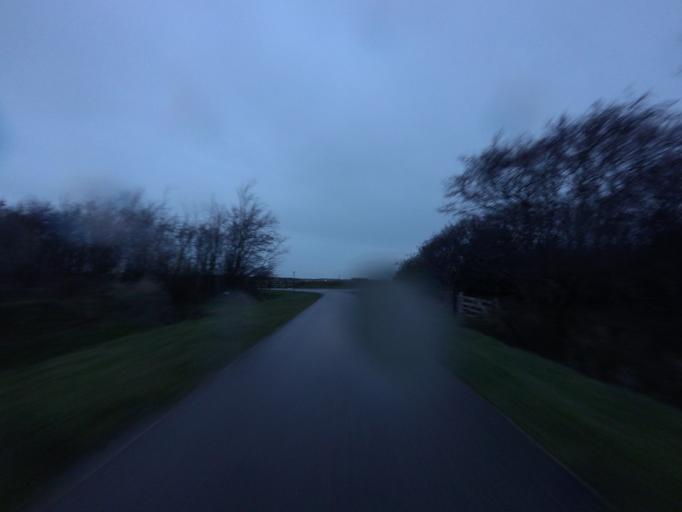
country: NL
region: North Holland
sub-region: Gemeente Texel
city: Den Burg
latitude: 53.0678
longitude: 4.7926
